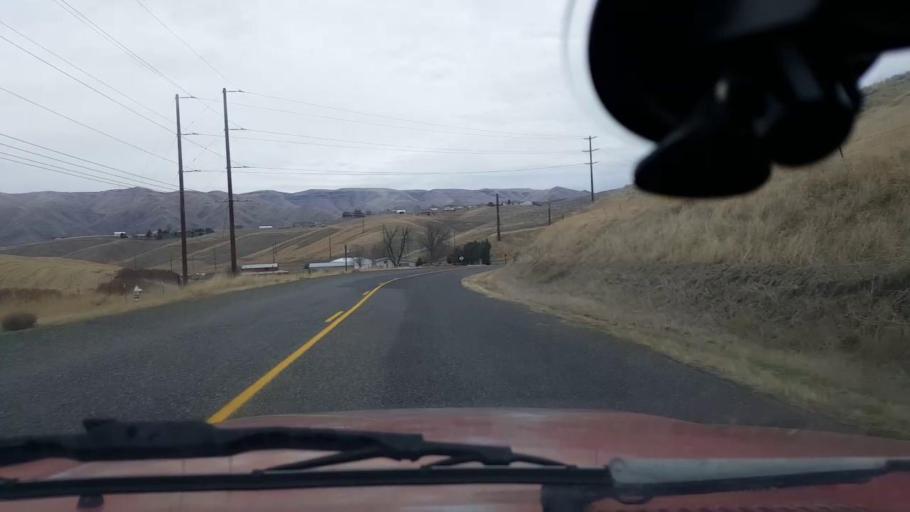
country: US
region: Washington
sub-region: Asotin County
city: Clarkston Heights-Vineland
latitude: 46.3975
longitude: -117.1027
